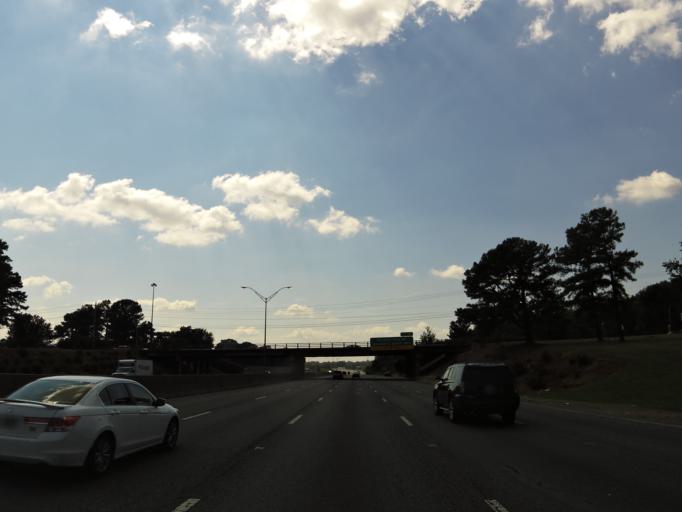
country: US
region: North Carolina
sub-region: Mecklenburg County
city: Charlotte
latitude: 35.2715
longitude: -80.8529
